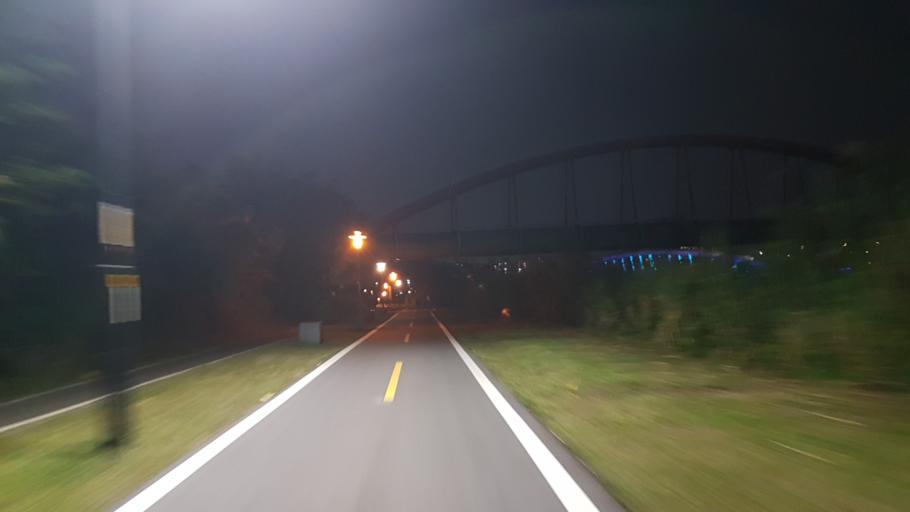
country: TW
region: Taipei
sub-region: Taipei
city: Banqiao
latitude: 24.9738
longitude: 121.5237
